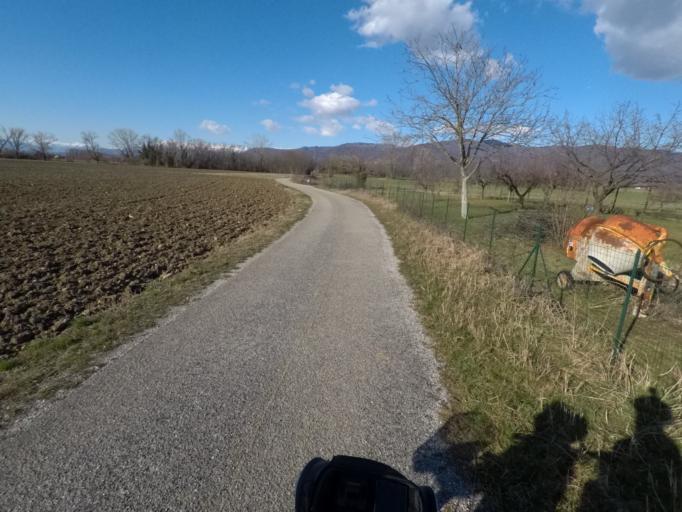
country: IT
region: Friuli Venezia Giulia
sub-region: Provincia di Udine
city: Moimacco
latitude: 46.0979
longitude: 13.3890
